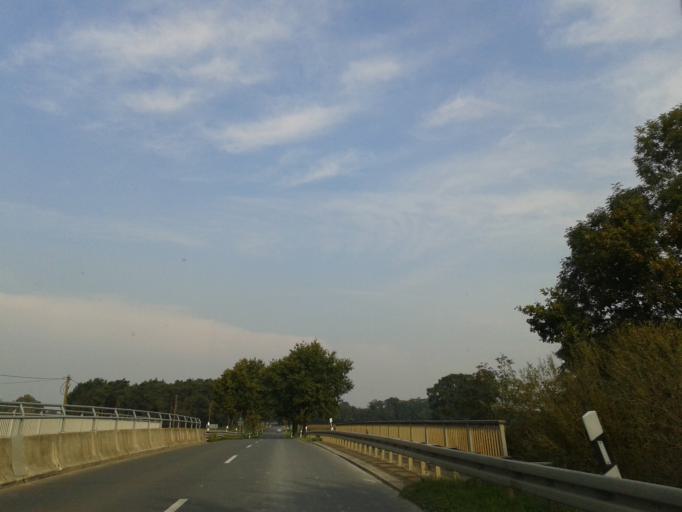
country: DE
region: North Rhine-Westphalia
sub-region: Regierungsbezirk Detmold
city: Hovelhof
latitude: 51.7485
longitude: 8.6311
